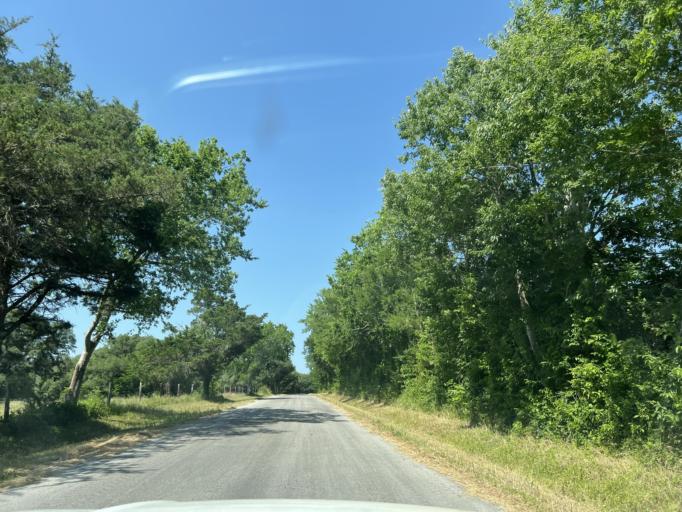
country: US
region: Texas
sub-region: Washington County
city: Brenham
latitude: 30.1708
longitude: -96.5049
